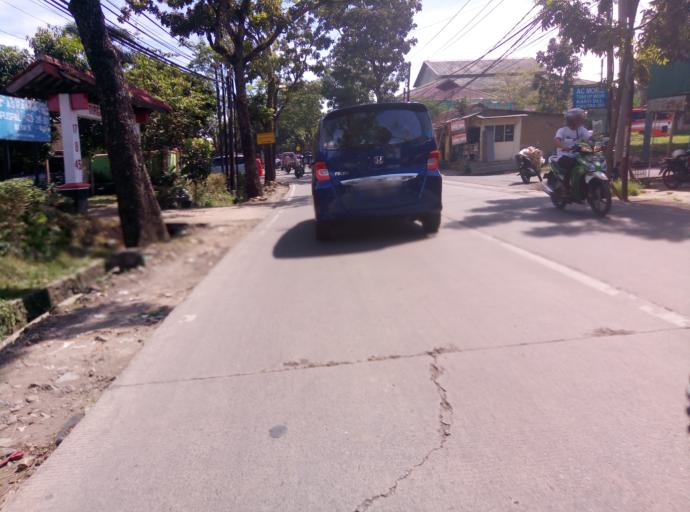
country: ID
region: West Java
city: Bandung
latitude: -6.8943
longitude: 107.6414
